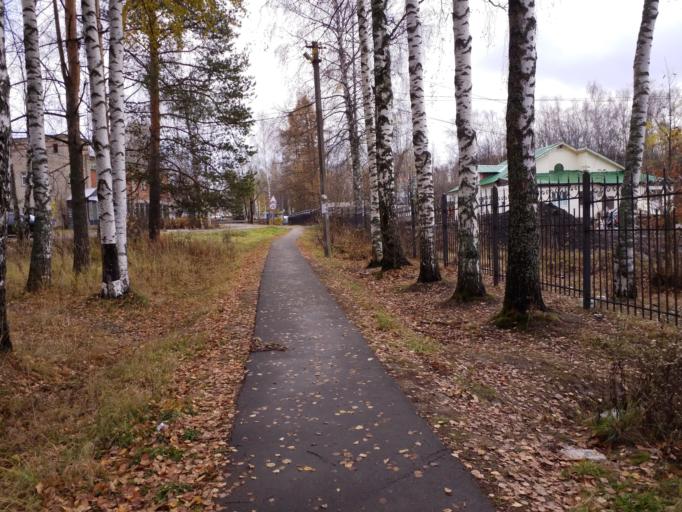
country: RU
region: Moskovskaya
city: Ashukino
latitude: 56.1627
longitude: 37.9435
